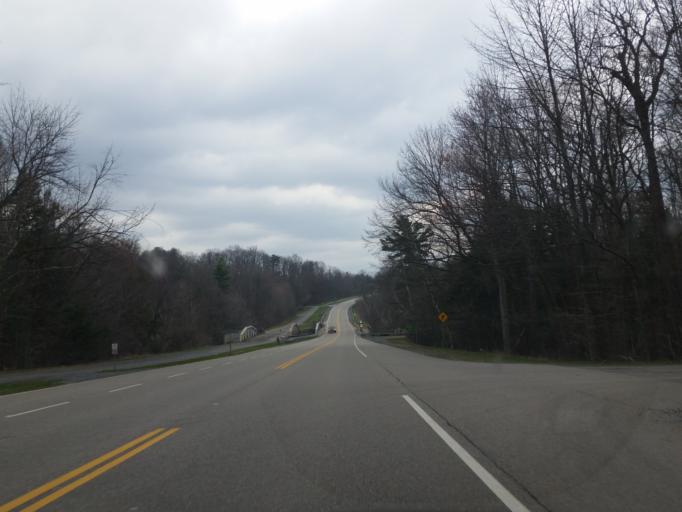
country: CA
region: Ontario
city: Brockville
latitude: 44.5019
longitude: -75.8071
